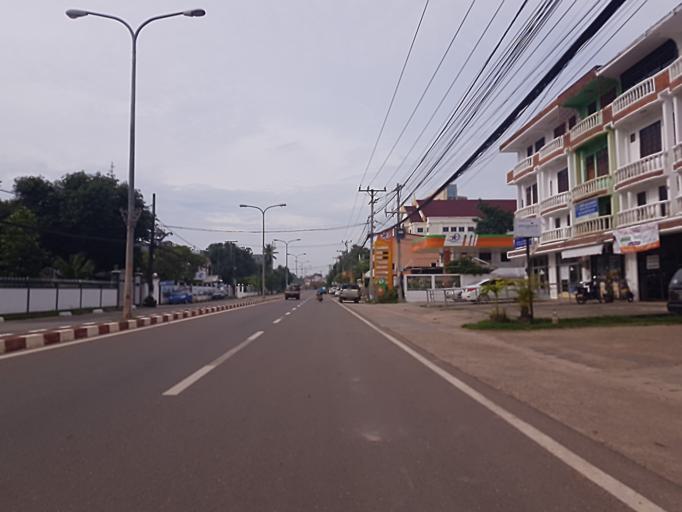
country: LA
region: Vientiane
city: Vientiane
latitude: 17.9455
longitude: 102.6198
